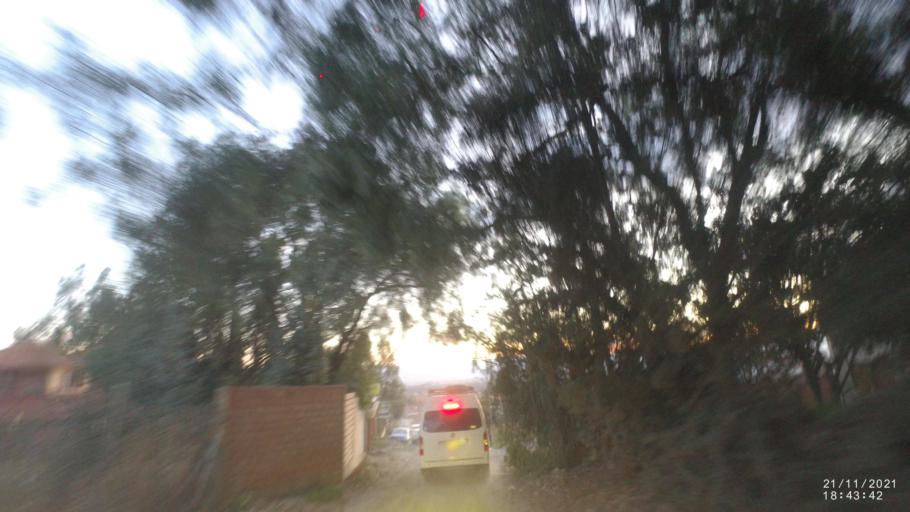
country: BO
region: Cochabamba
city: Cochabamba
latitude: -17.3225
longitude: -66.2169
